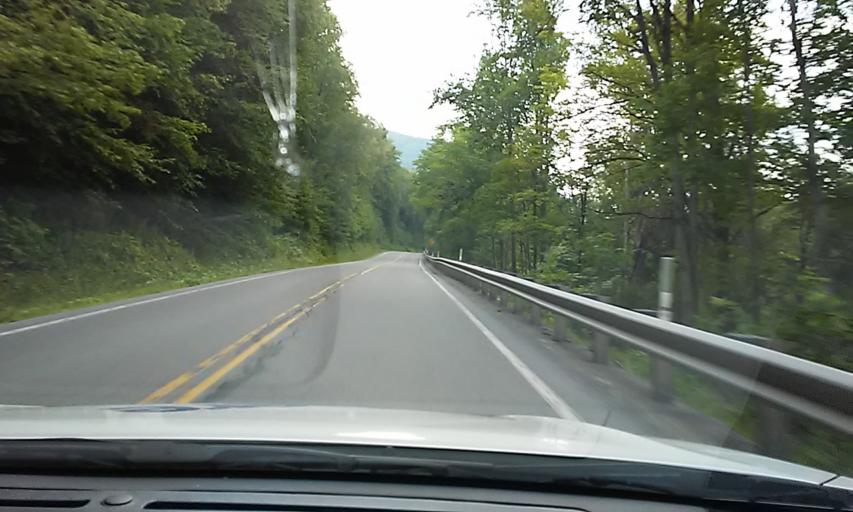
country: US
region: Pennsylvania
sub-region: Potter County
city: Galeton
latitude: 41.7983
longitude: -77.7695
